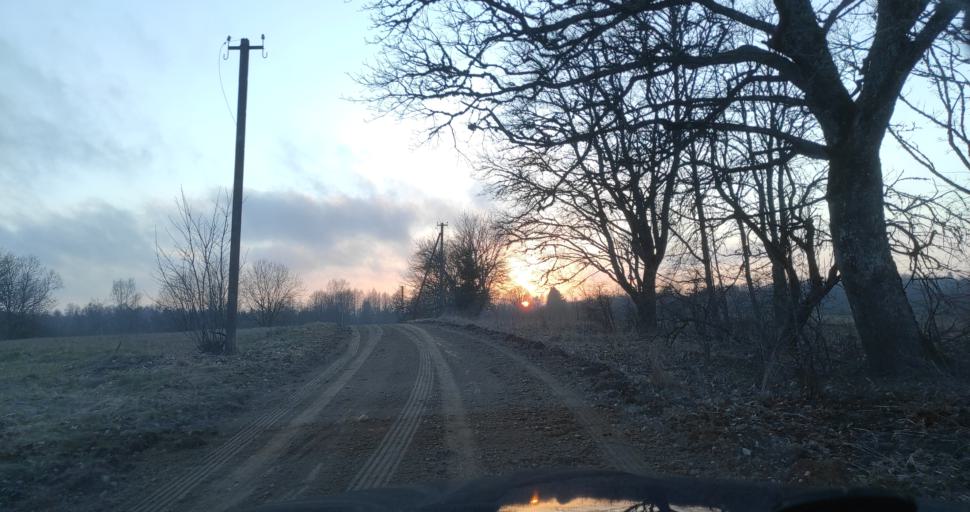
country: LV
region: Kuldigas Rajons
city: Kuldiga
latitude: 56.8154
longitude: 21.8091
